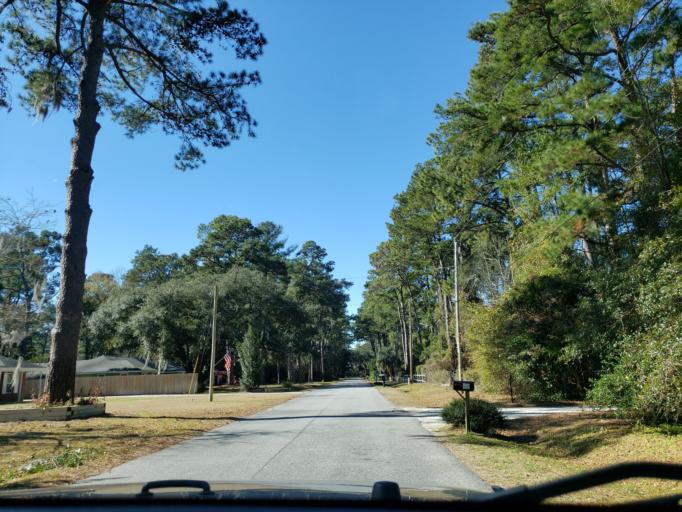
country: US
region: Georgia
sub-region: Chatham County
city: Wilmington Island
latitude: 32.0393
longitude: -80.9734
